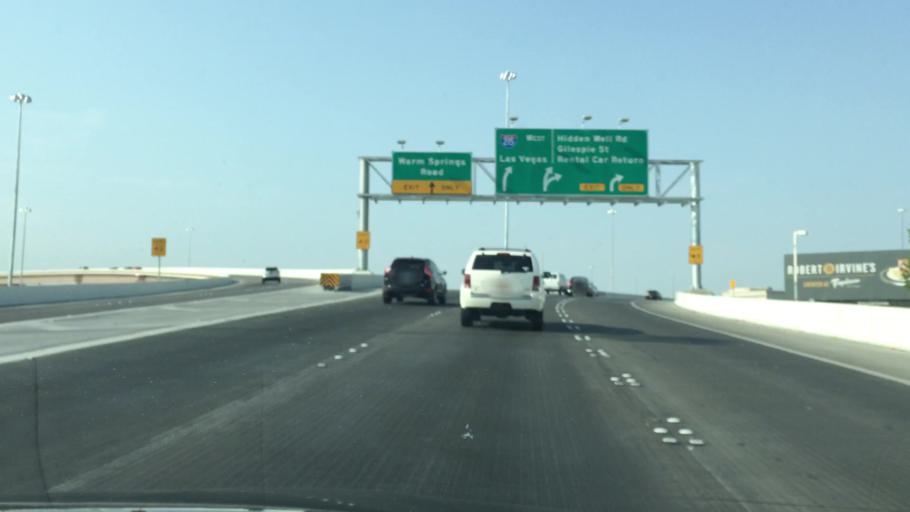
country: US
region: Nevada
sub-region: Clark County
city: Paradise
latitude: 36.0655
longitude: -115.1489
